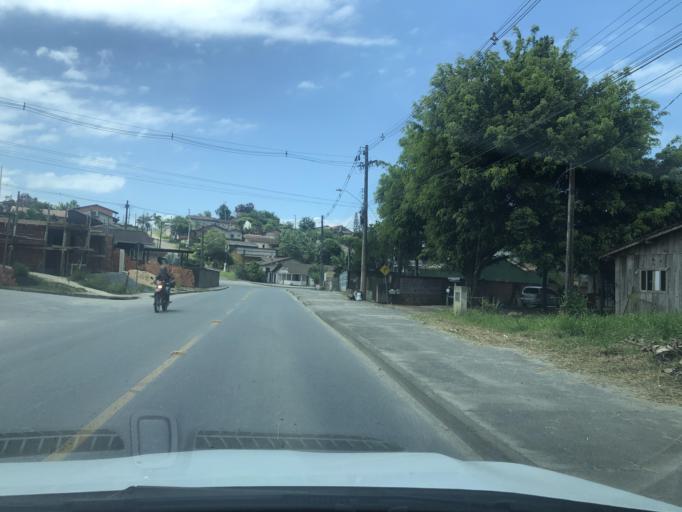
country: BR
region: Santa Catarina
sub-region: Joinville
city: Joinville
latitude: -26.3544
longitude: -48.7884
